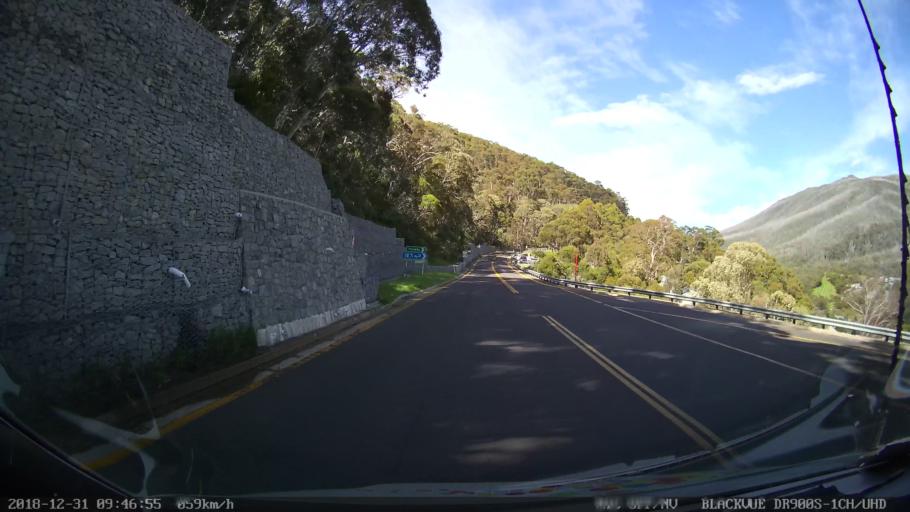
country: AU
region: New South Wales
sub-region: Snowy River
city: Jindabyne
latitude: -36.5062
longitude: 148.3059
